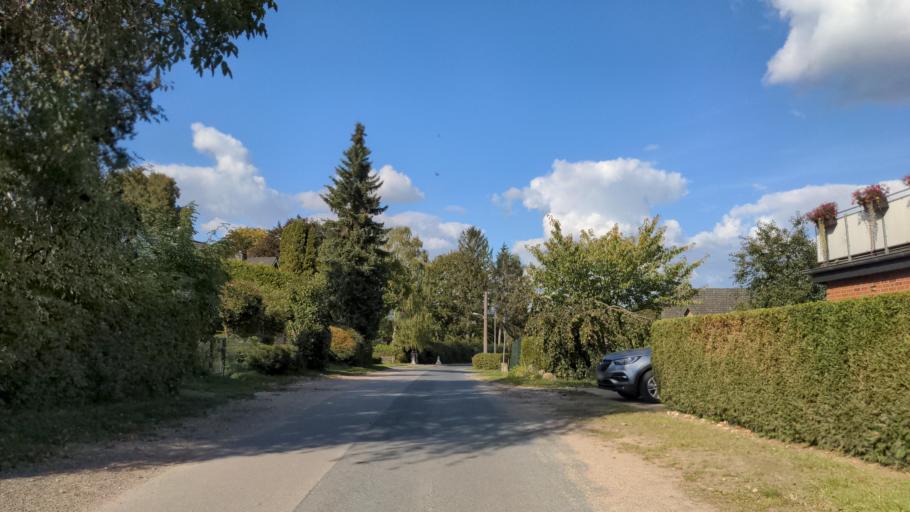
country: DE
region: Schleswig-Holstein
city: Monkhagen
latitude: 53.9127
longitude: 10.5980
